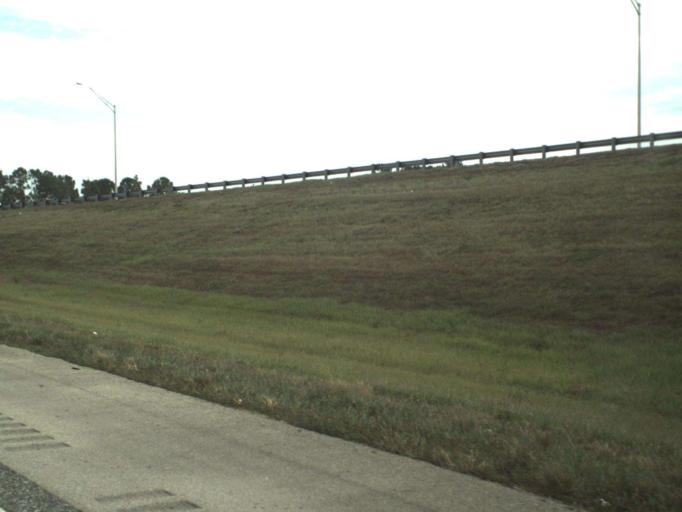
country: US
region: Florida
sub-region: Saint Lucie County
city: Port Saint Lucie
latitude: 27.2108
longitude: -80.4003
